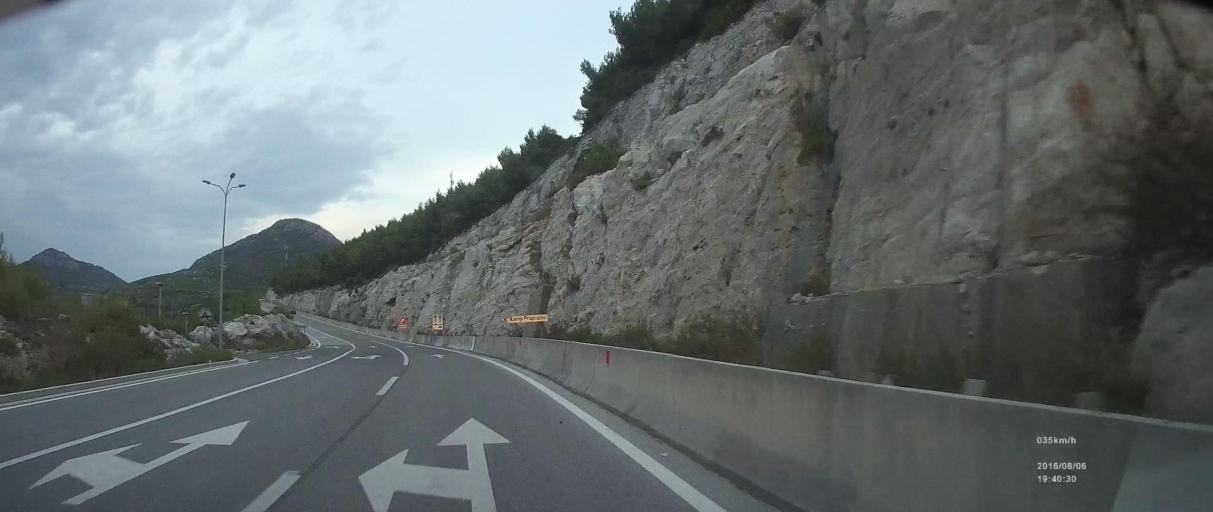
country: HR
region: Dubrovacko-Neretvanska
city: Ston
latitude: 42.8141
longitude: 17.6796
